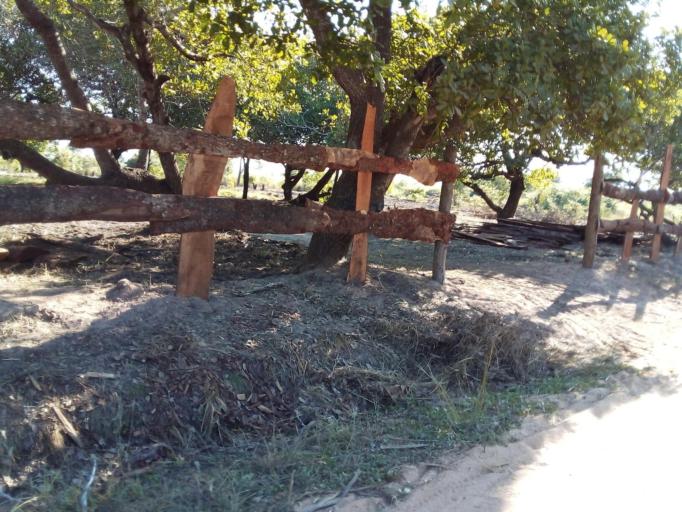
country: MZ
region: Zambezia
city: Quelimane
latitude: -17.5370
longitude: 36.6228
